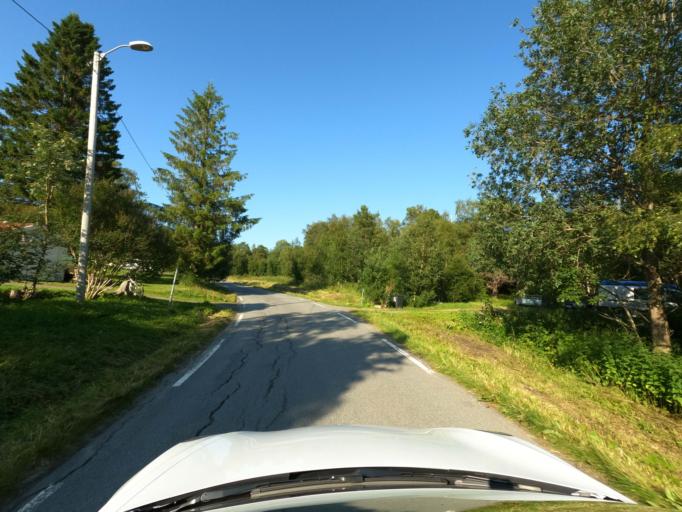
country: NO
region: Nordland
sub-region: Narvik
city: Narvik
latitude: 68.4725
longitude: 17.5076
